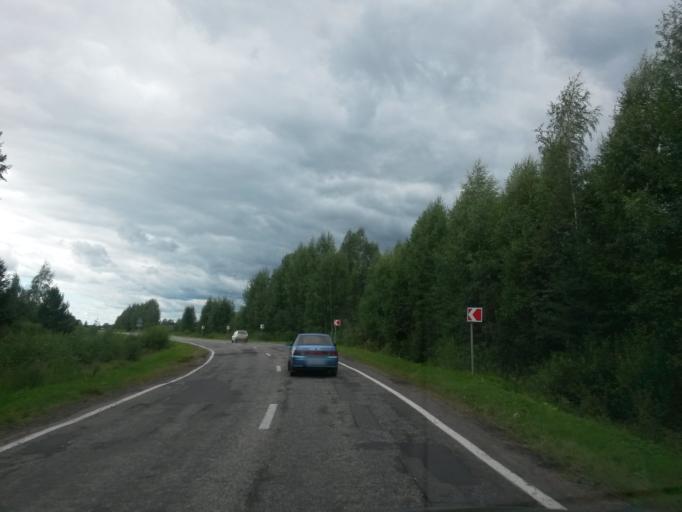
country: RU
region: Jaroslavl
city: Konstantinovskiy
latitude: 57.8051
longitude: 39.7786
